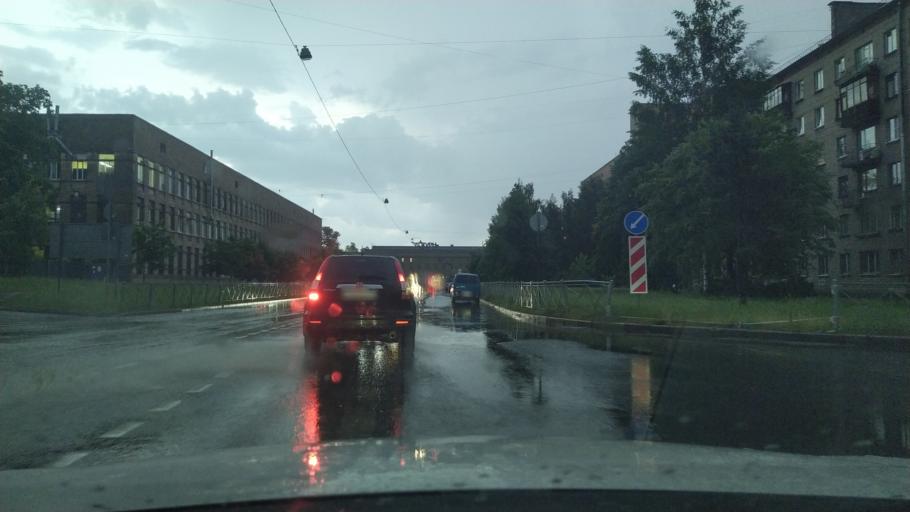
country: RU
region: Leningrad
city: Sampsonievskiy
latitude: 59.9805
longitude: 30.3542
